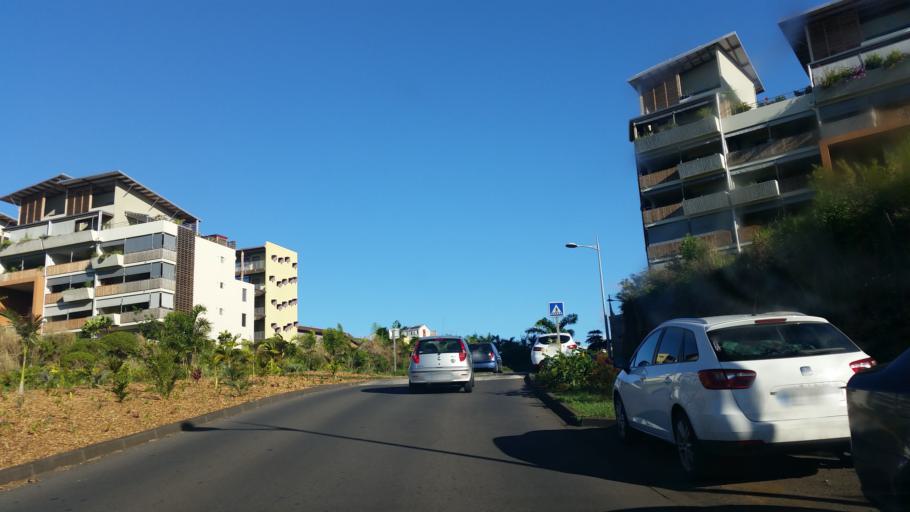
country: RE
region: Reunion
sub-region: Reunion
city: Sainte-Marie
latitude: -20.9171
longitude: 55.5255
